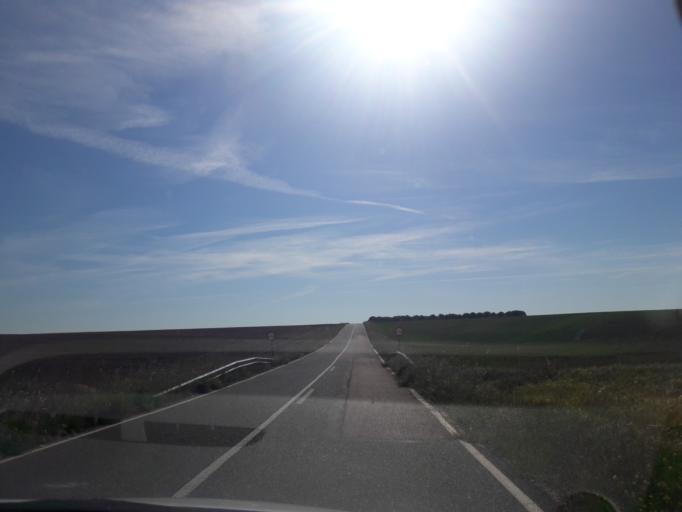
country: ES
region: Castille and Leon
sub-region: Provincia de Salamanca
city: Aldeanueva de Figueroa
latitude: 41.1372
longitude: -5.4977
